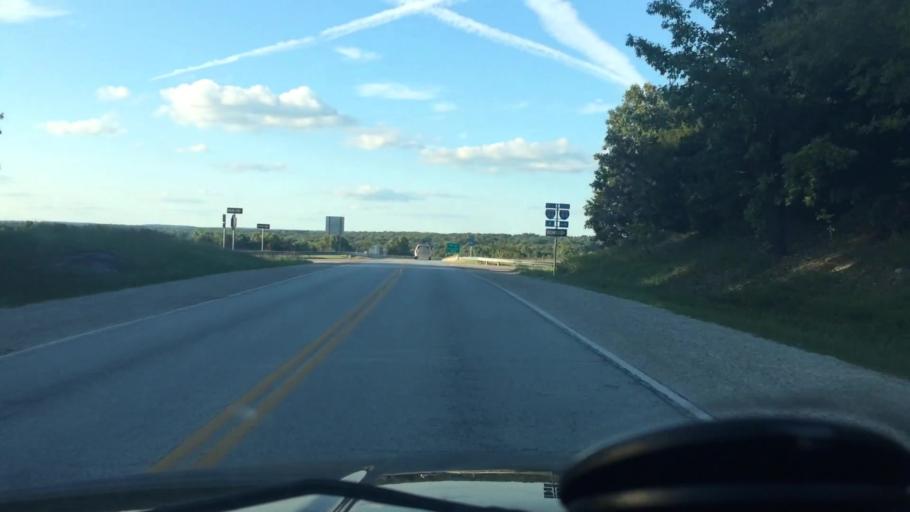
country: US
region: Missouri
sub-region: Webster County
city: Marshfield
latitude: 37.3001
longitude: -92.9996
